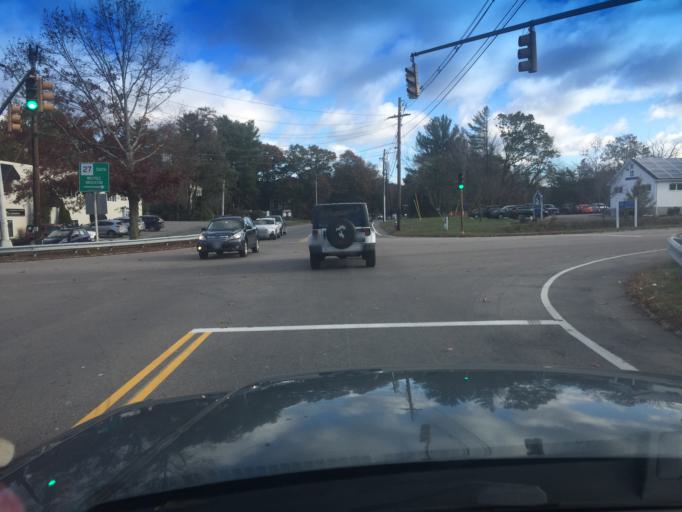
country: US
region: Massachusetts
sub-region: Norfolk County
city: Medfield
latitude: 42.1921
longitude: -71.3241
